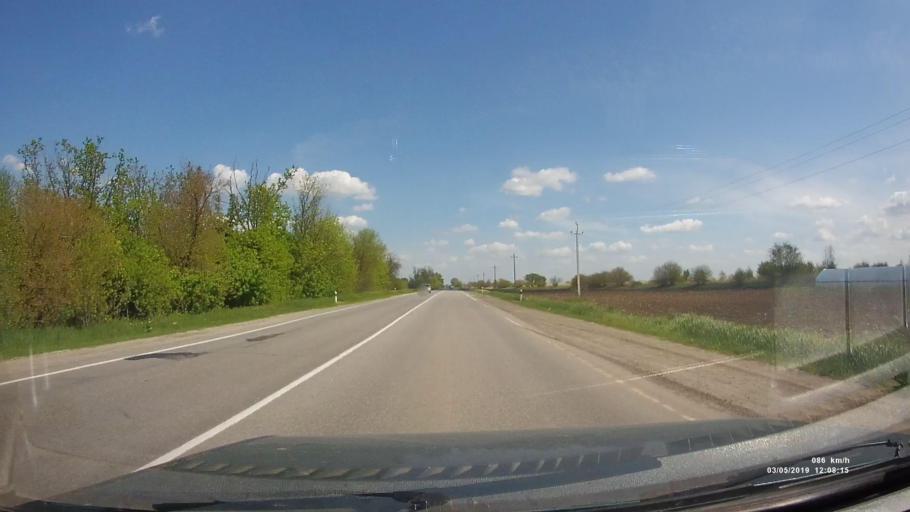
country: RU
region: Rostov
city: Bagayevskaya
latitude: 47.2865
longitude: 40.4933
